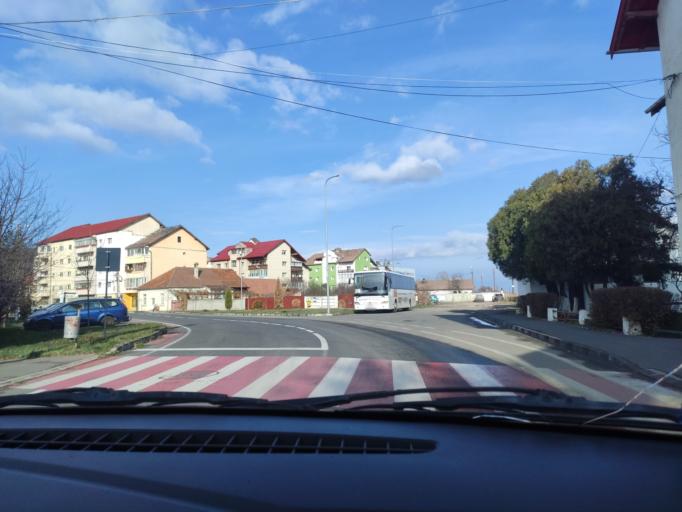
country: RO
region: Brasov
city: Codlea
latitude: 45.6935
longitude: 25.4568
